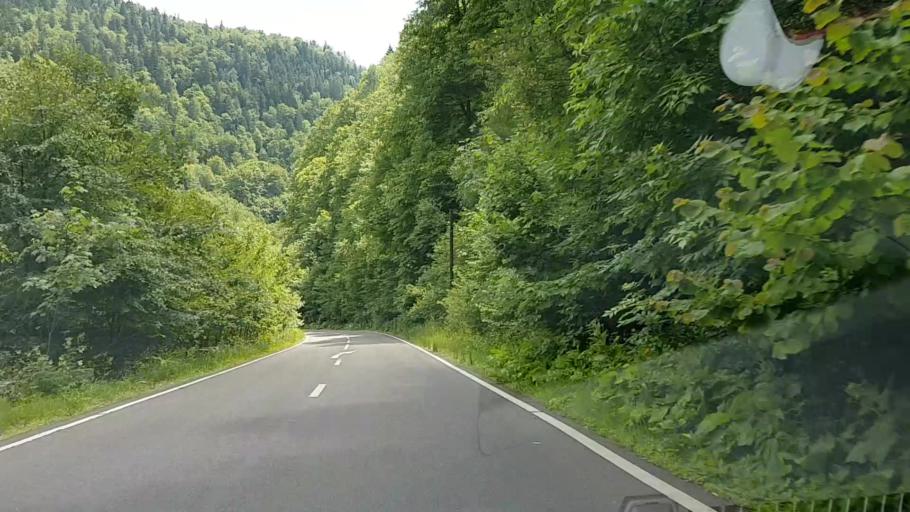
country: RO
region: Suceava
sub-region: Comuna Crucea
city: Crucea
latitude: 47.3132
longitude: 25.6269
